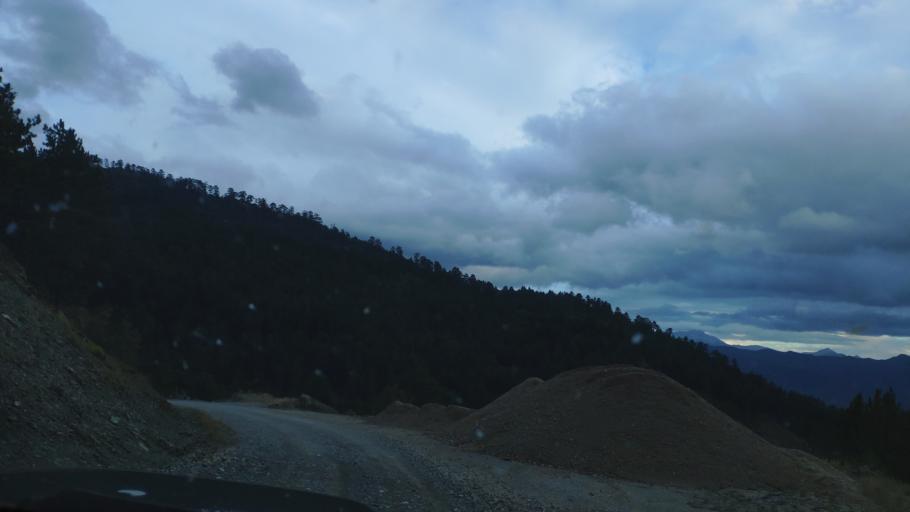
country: AL
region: Korce
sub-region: Rrethi i Kolonjes
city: Erseke
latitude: 40.2893
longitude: 20.8599
